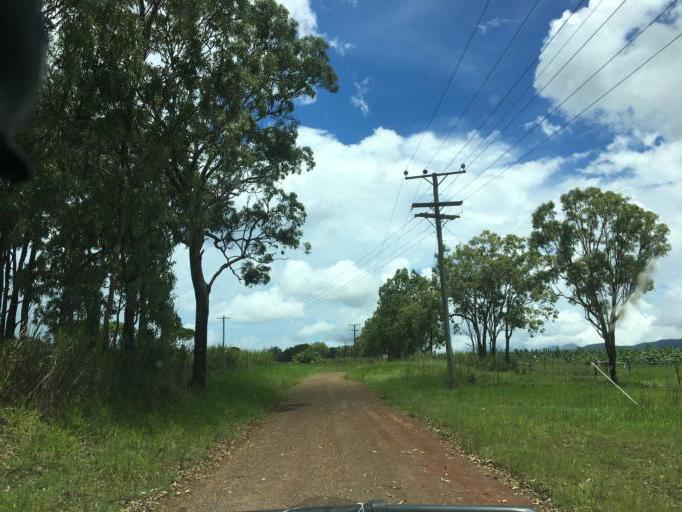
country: AU
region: Queensland
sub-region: Tablelands
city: Mareeba
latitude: -16.9909
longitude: 145.5231
